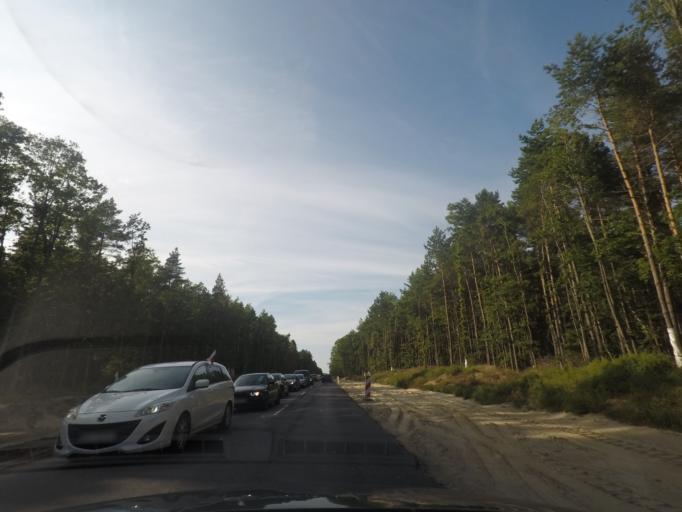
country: PL
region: Pomeranian Voivodeship
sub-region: Powiat leborski
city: Leba
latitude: 54.7037
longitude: 17.5850
